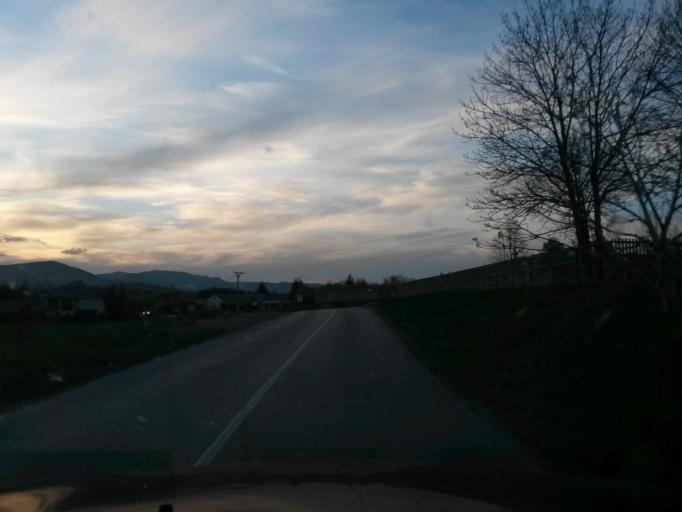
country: HU
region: Borsod-Abauj-Zemplen
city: Satoraljaujhely
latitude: 48.5182
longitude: 21.5950
